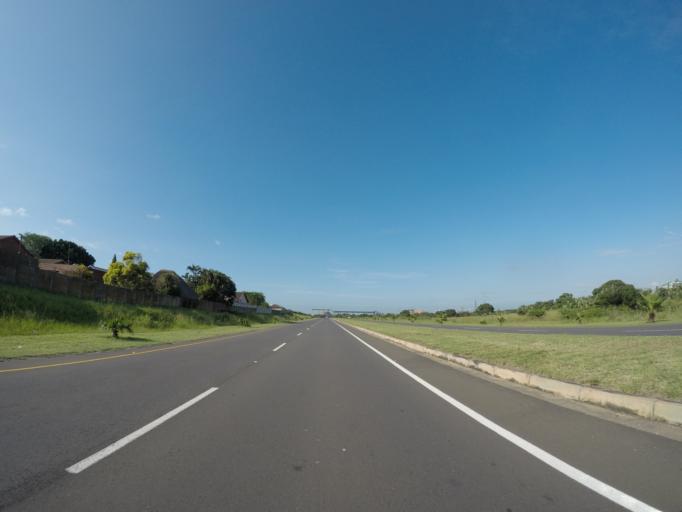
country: ZA
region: KwaZulu-Natal
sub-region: uThungulu District Municipality
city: Richards Bay
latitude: -28.7618
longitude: 32.0503
